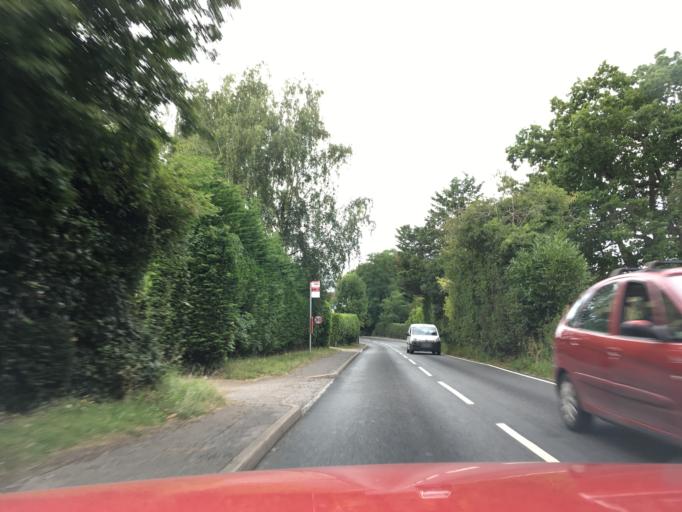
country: GB
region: England
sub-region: Kent
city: Marden
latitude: 51.1147
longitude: 0.4679
